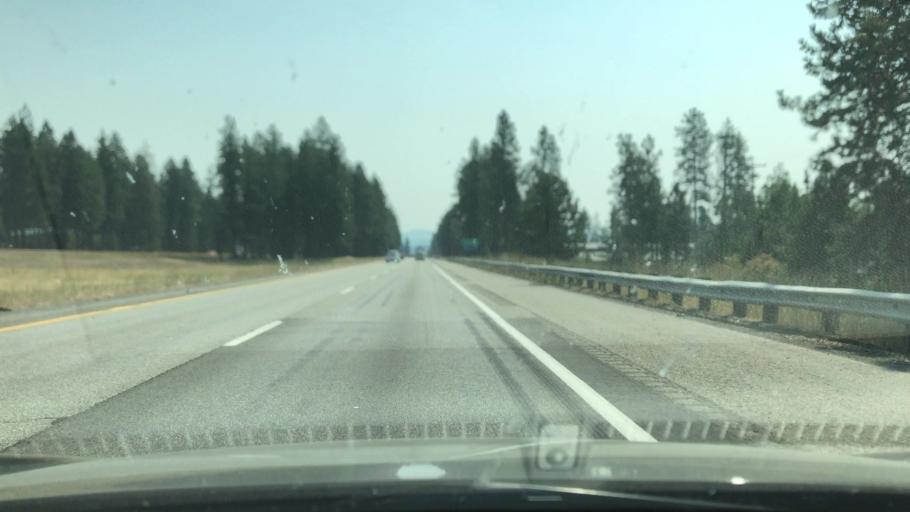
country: US
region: Idaho
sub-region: Kootenai County
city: Coeur d'Alene
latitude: 47.7071
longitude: -116.8500
